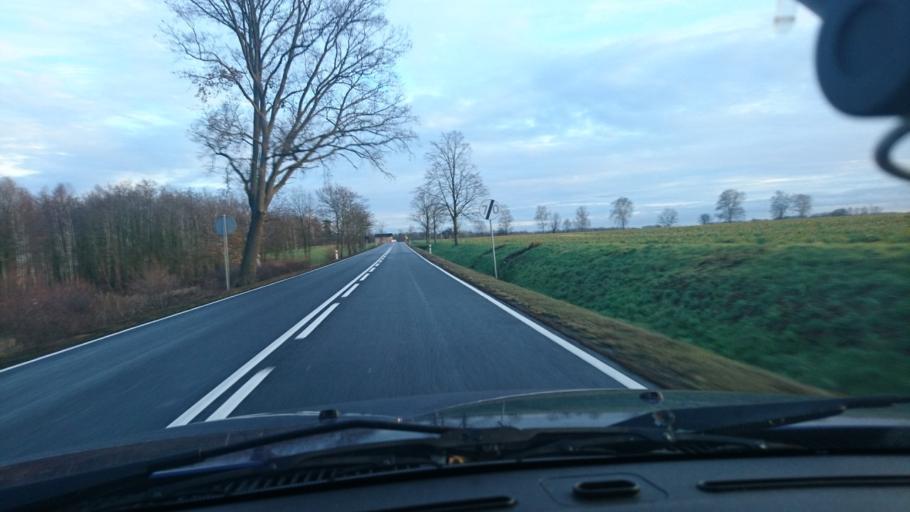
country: PL
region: Lodz Voivodeship
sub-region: Powiat wieruszowski
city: Boleslawiec
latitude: 51.1551
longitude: 18.1755
